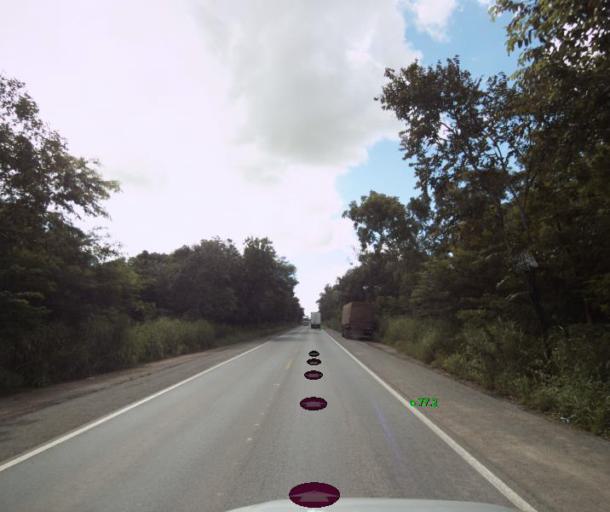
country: BR
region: Goias
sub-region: Porangatu
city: Porangatu
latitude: -13.4945
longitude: -49.1331
